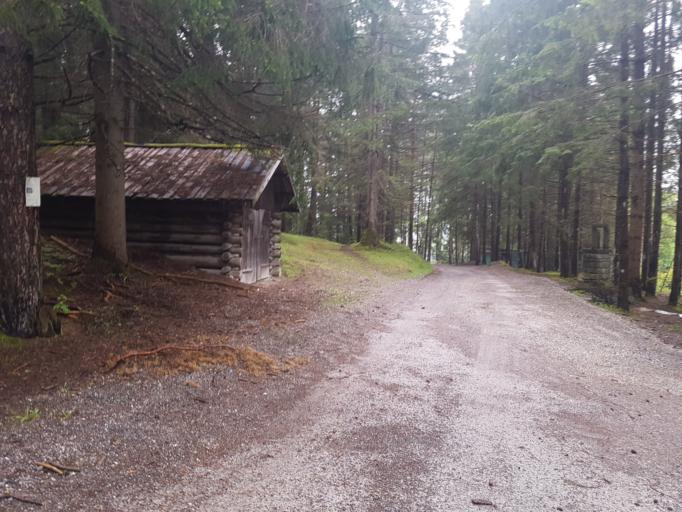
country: AT
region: Tyrol
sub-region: Politischer Bezirk Imst
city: Obsteig
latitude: 47.3044
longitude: 10.9211
